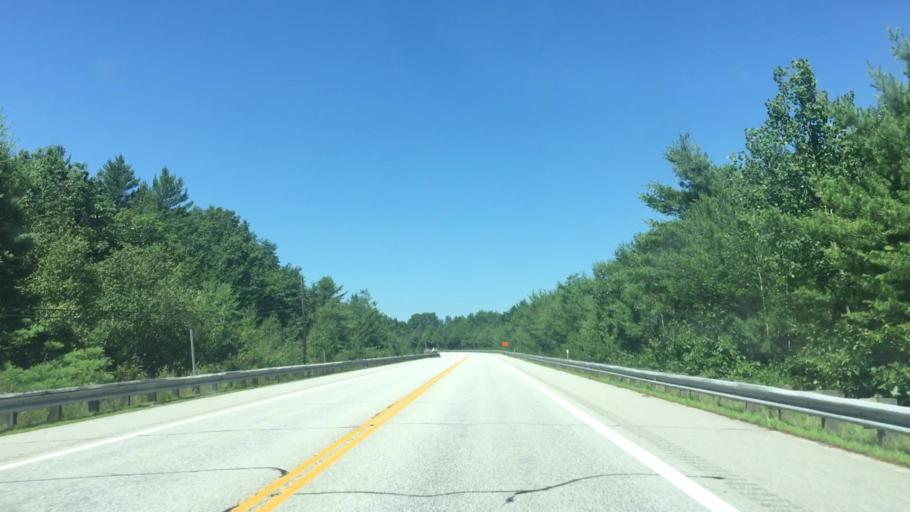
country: US
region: New Hampshire
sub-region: Merrimack County
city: Hopkinton
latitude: 43.1785
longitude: -71.7025
